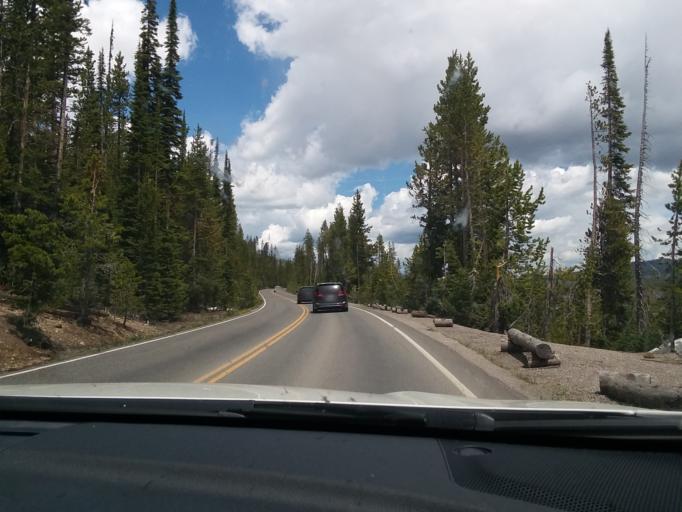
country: US
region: Montana
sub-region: Gallatin County
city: West Yellowstone
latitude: 44.2068
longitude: -110.6609
